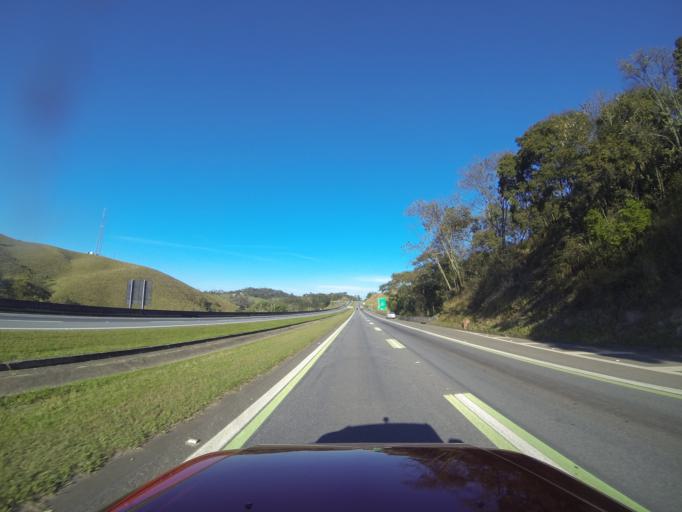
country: BR
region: Sao Paulo
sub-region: Santa Isabel
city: Santa Isabel
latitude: -23.2000
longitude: -46.1752
